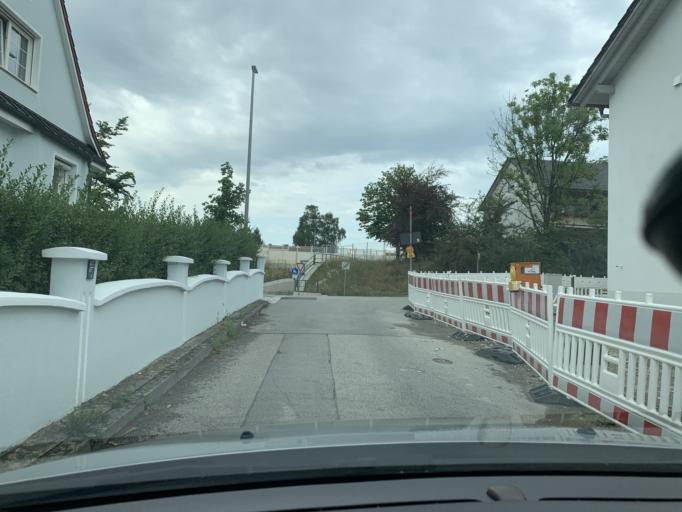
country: DE
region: Bavaria
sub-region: Upper Bavaria
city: Muehldorf
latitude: 48.2470
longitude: 12.5348
